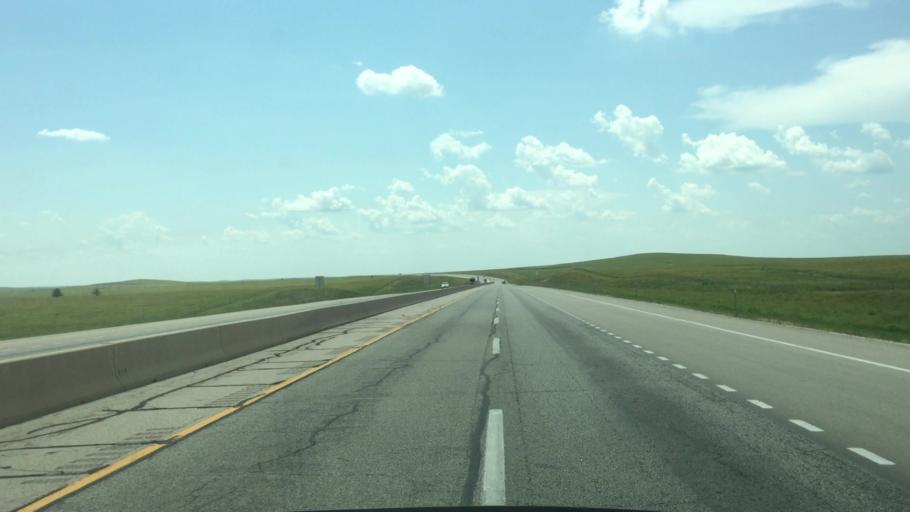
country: US
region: Kansas
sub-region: Chase County
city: Cottonwood Falls
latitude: 38.2285
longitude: -96.4136
